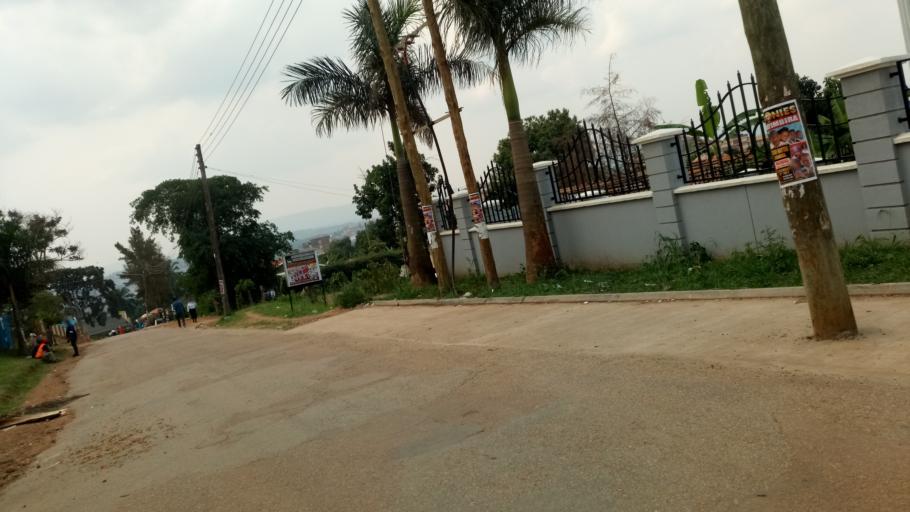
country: UG
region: Western Region
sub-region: Mbarara District
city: Mbarara
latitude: -0.6101
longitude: 30.6593
